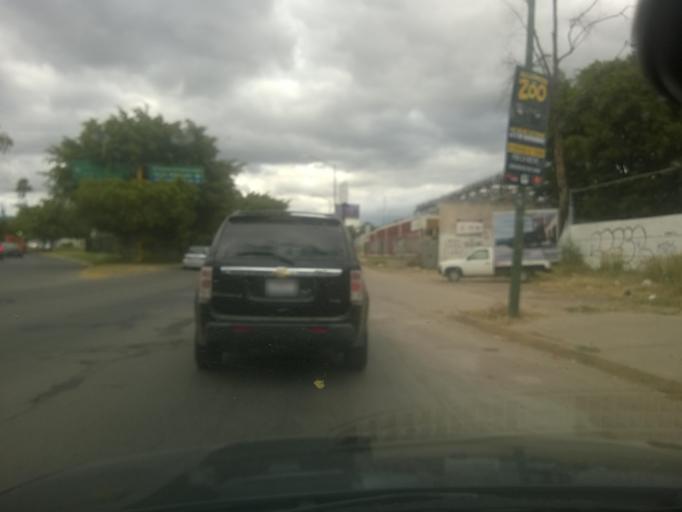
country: MX
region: Guanajuato
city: Leon
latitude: 21.1537
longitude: -101.6843
